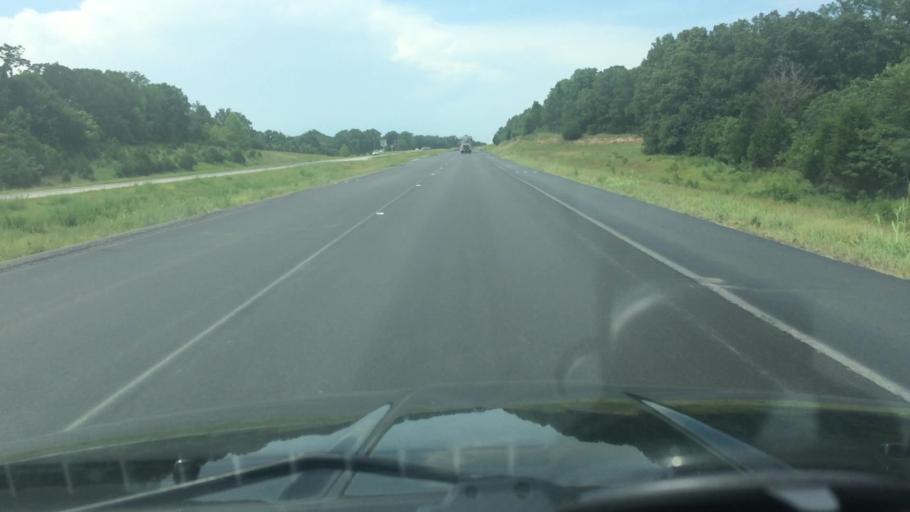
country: US
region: Missouri
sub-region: Saint Clair County
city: Osceola
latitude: 37.9473
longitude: -93.6374
